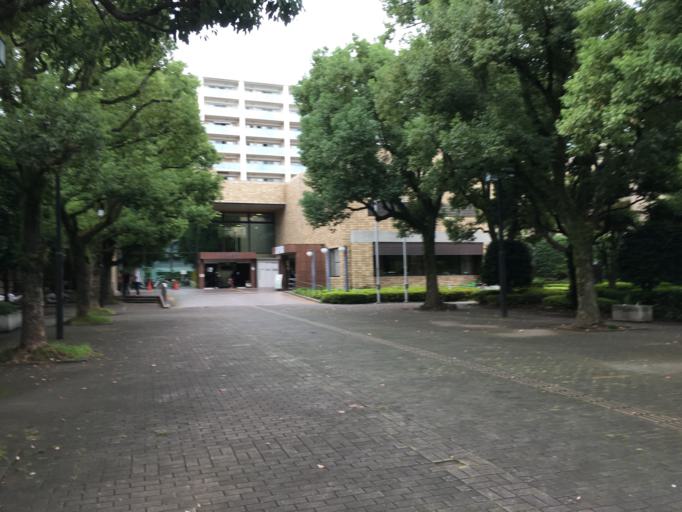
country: JP
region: Kumamoto
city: Kumamoto
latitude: 32.7990
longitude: 130.7245
